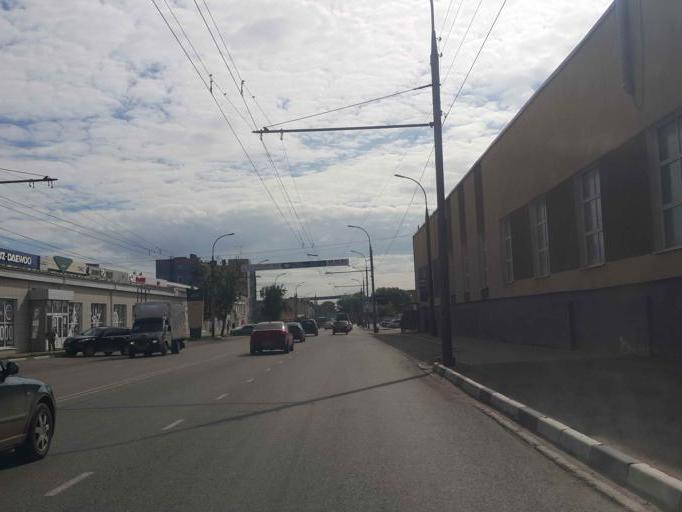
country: RU
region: Tambov
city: Tambov
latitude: 52.7239
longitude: 41.4327
